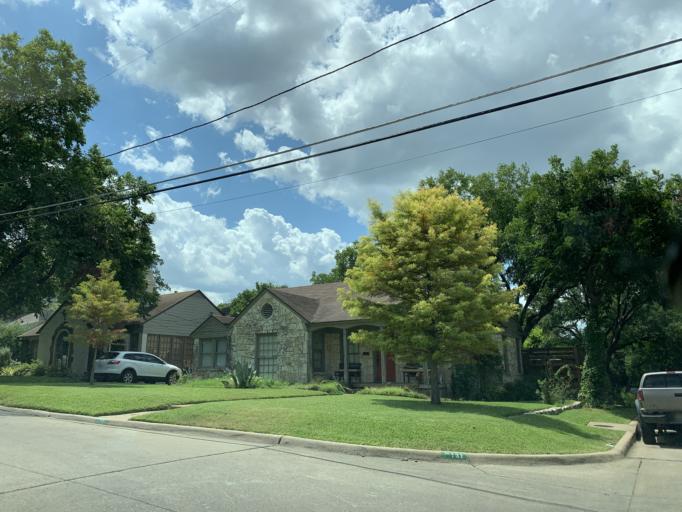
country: US
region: Texas
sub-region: Dallas County
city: Cockrell Hill
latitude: 32.7522
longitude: -96.8556
